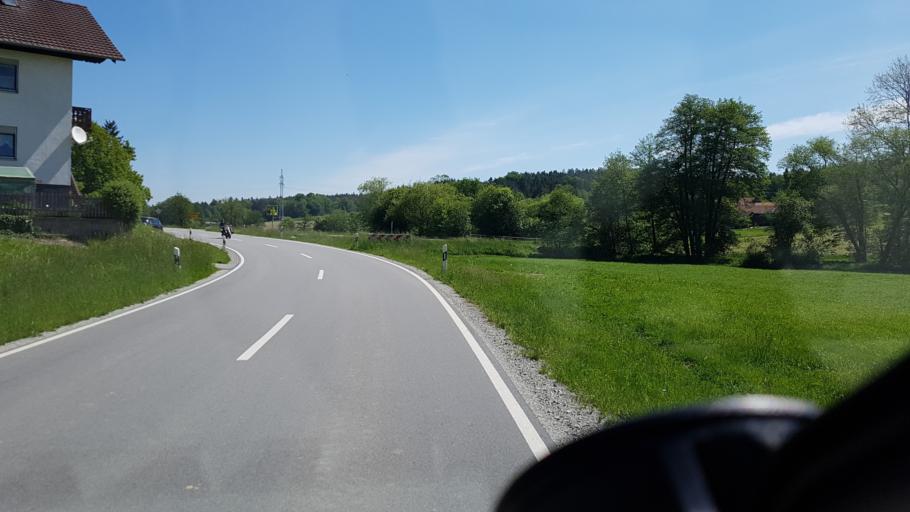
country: DE
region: Bavaria
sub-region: Lower Bavaria
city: Postmunster
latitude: 48.3890
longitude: 12.9159
